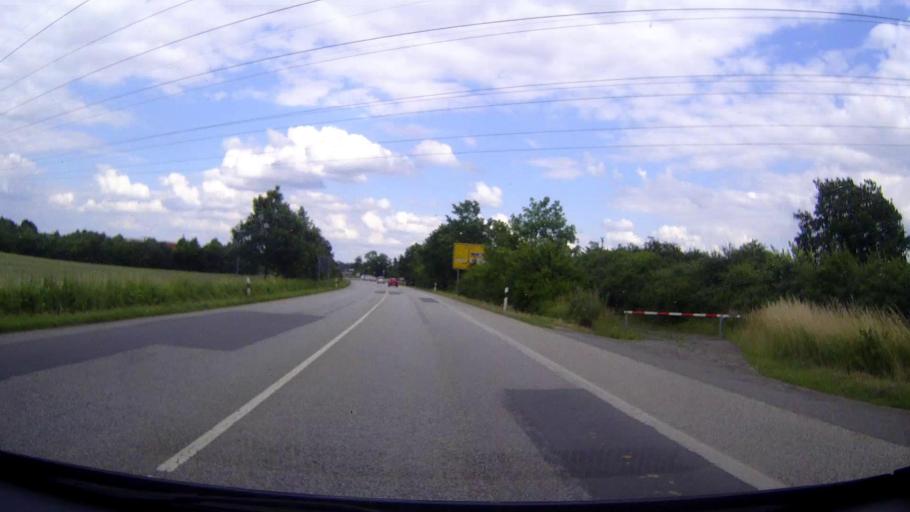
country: DE
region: Schleswig-Holstein
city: Stockelsdorf
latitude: 53.8913
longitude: 10.6142
